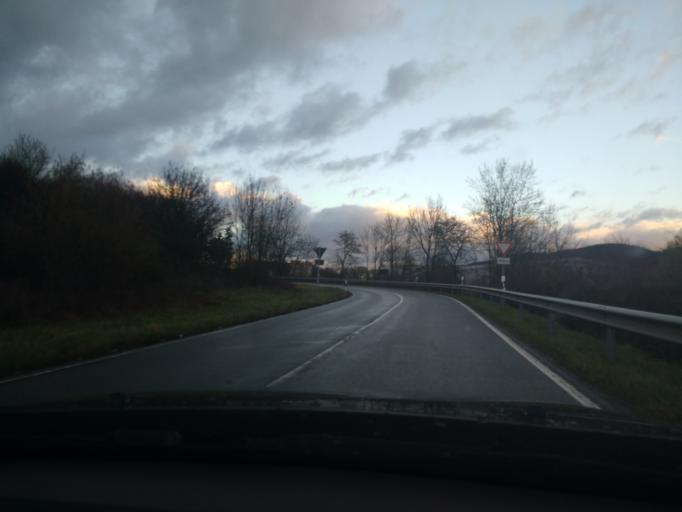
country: DE
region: Rheinland-Pfalz
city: Schweich
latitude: 49.8187
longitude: 6.7424
